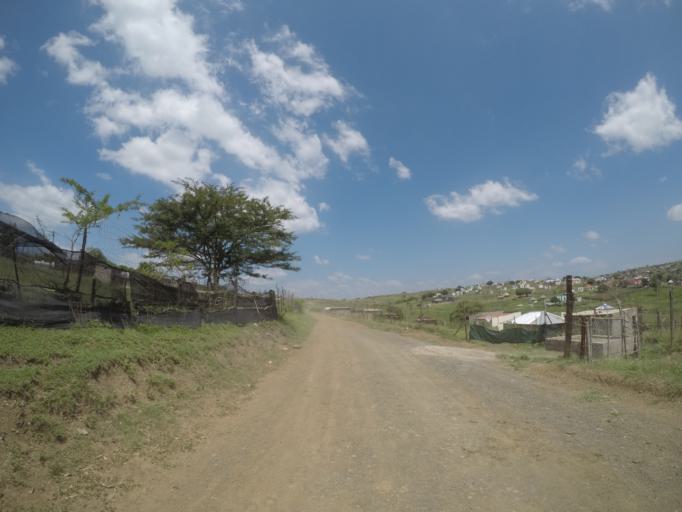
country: ZA
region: KwaZulu-Natal
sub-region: uThungulu District Municipality
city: Empangeni
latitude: -28.6051
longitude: 31.7407
